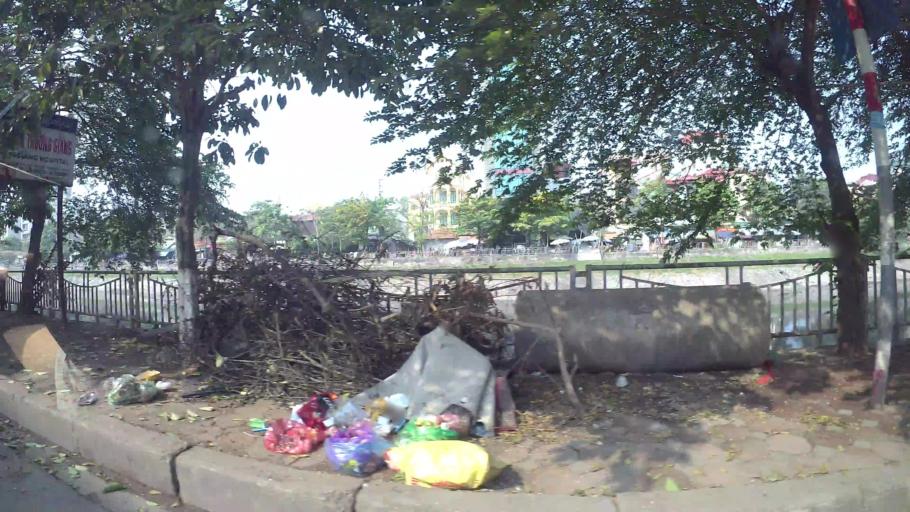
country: VN
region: Ha Noi
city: Thanh Xuan
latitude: 20.9805
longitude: 105.8184
